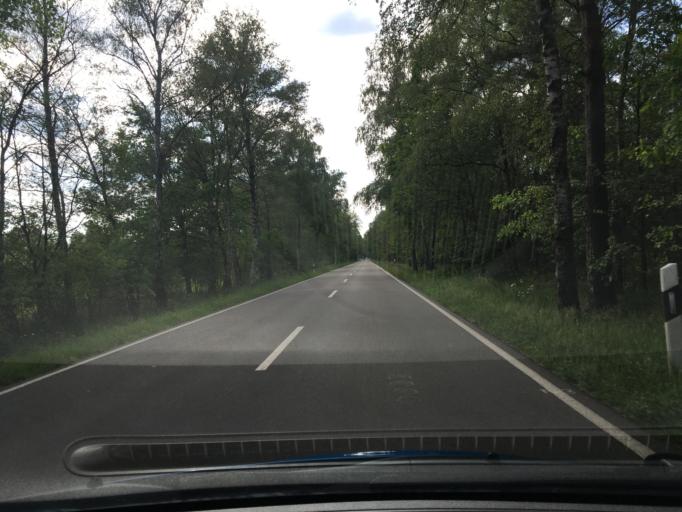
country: DE
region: Lower Saxony
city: Wistedt
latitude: 53.2738
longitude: 9.6391
